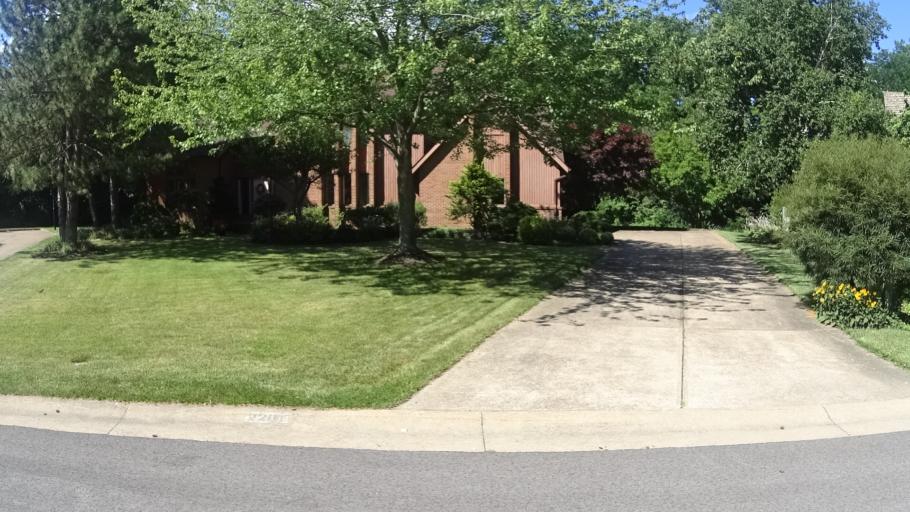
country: US
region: Ohio
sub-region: Erie County
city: Sandusky
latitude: 41.4070
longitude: -82.6513
